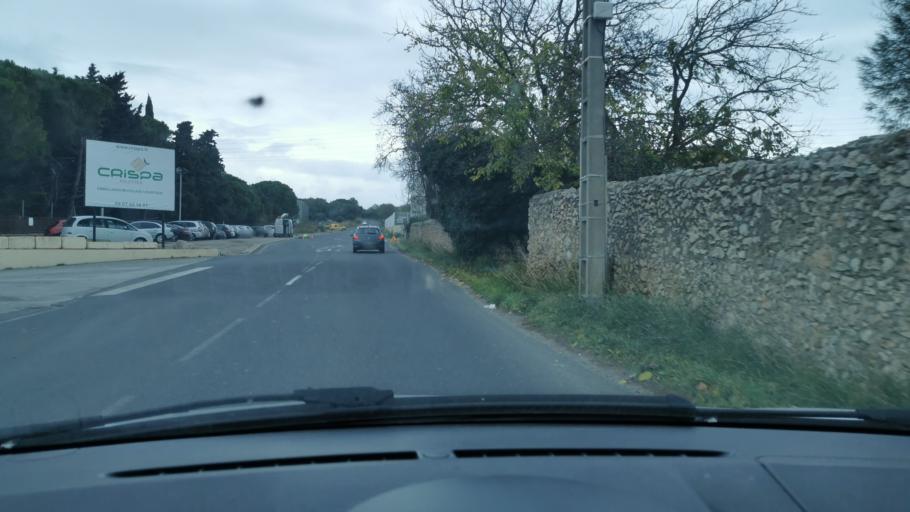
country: FR
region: Languedoc-Roussillon
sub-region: Departement de l'Herault
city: Balaruc-les-Bains
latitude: 43.4355
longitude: 3.7045
